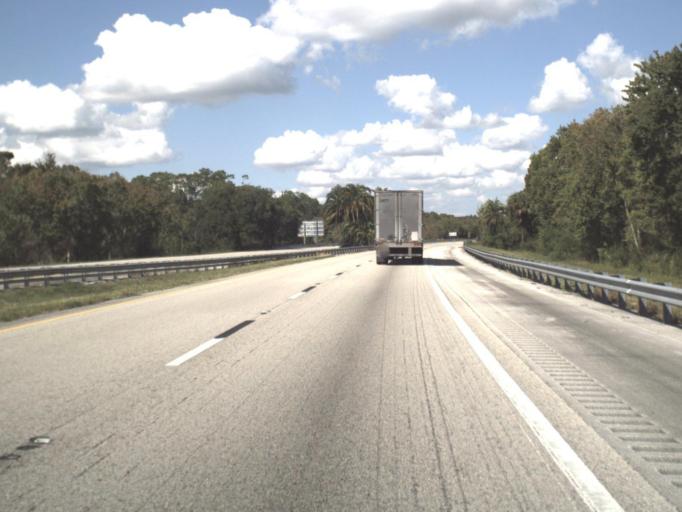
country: US
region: Florida
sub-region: Indian River County
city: Fellsmere
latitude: 27.6839
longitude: -80.8934
